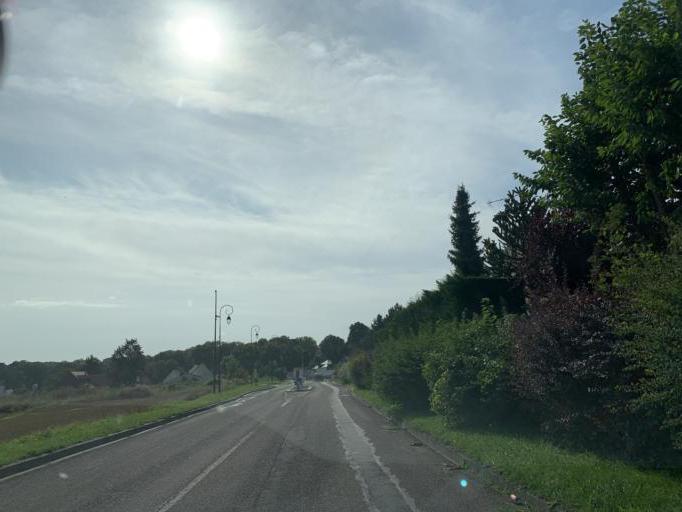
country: FR
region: Ile-de-France
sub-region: Departement de Seine-et-Marne
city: Annet-sur-Marne
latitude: 48.9313
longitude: 2.7166
